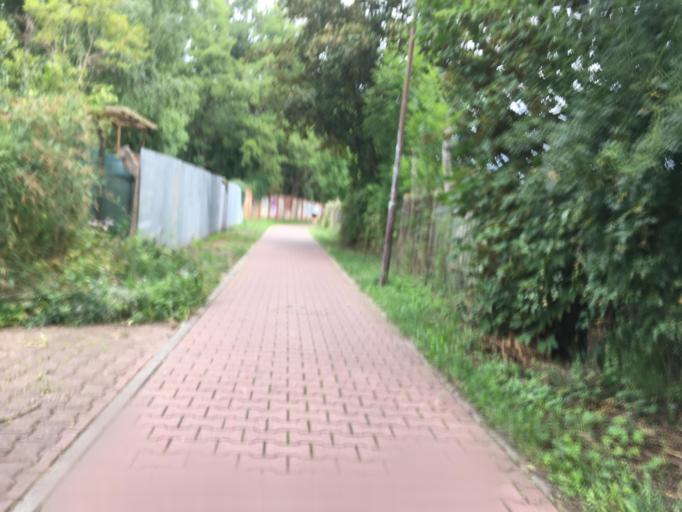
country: DE
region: Brandenburg
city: Prenzlau
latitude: 53.3072
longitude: 13.8456
